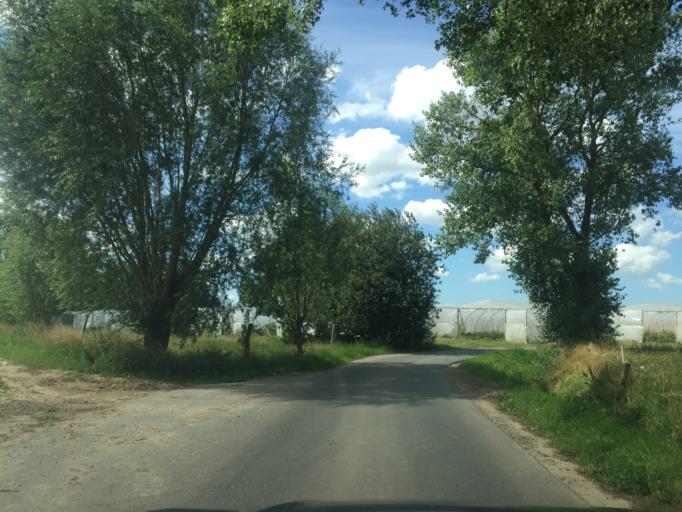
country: BE
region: Flanders
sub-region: Provincie West-Vlaanderen
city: Hooglede
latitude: 50.9781
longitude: 3.0553
